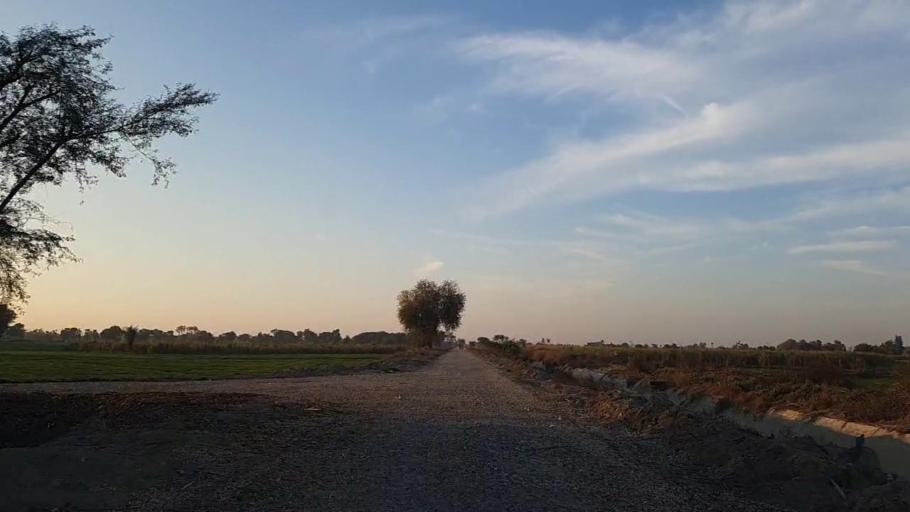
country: PK
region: Sindh
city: Bandhi
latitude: 26.6176
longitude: 68.3526
